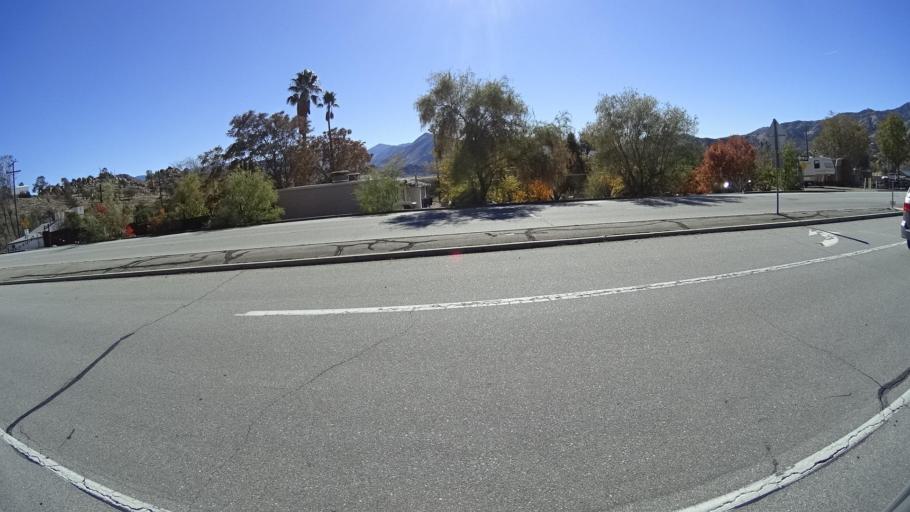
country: US
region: California
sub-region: Kern County
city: Wofford Heights
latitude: 35.7085
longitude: -118.4481
